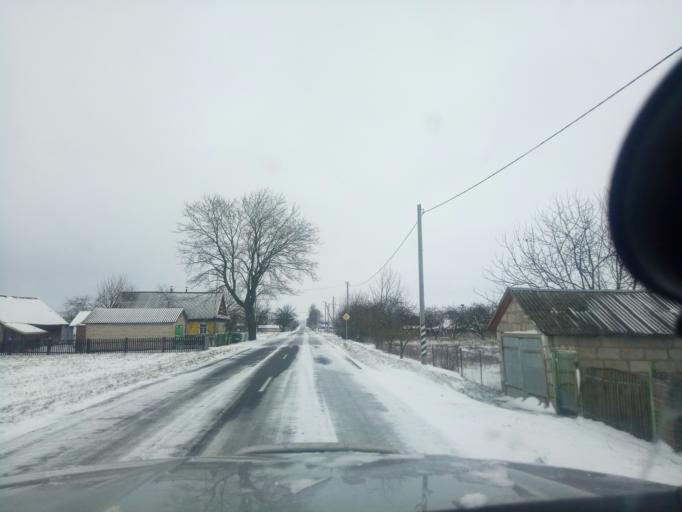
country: BY
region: Minsk
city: Klyetsk
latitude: 53.0531
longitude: 26.7715
